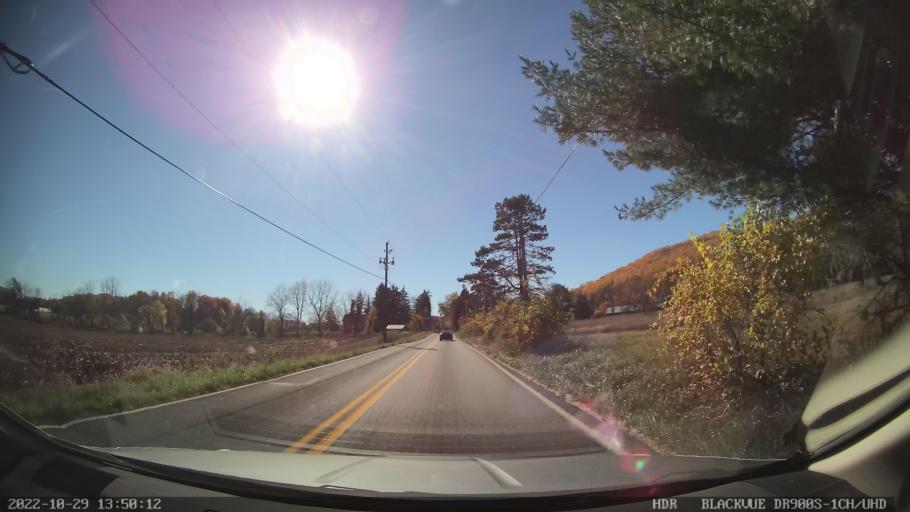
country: US
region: Pennsylvania
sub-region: Lehigh County
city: Emmaus
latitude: 40.5366
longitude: -75.4580
